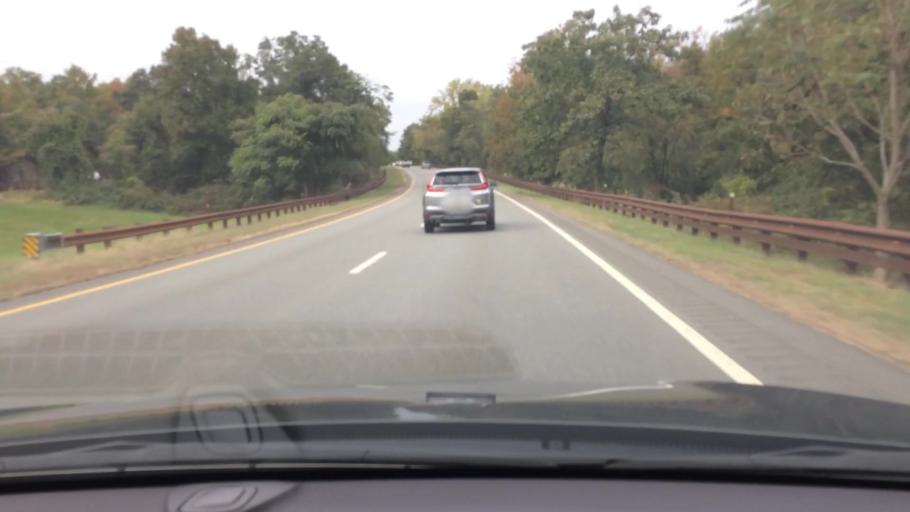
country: US
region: New Jersey
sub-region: Bergen County
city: Englewood Cliffs
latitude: 40.9105
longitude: -73.9336
